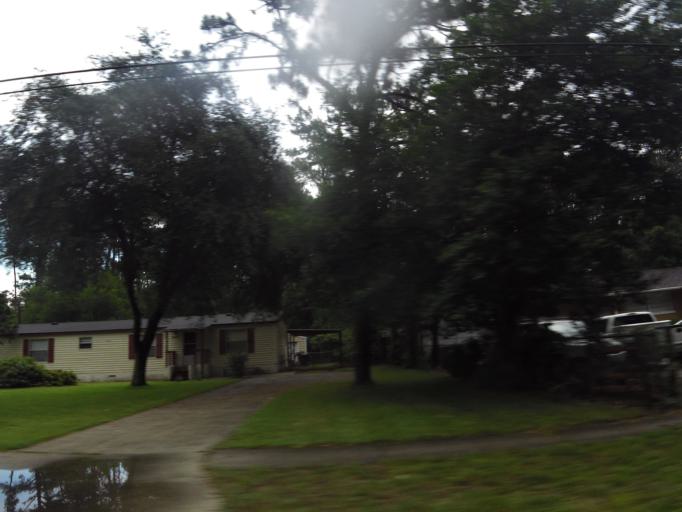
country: US
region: Florida
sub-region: Duval County
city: Jacksonville
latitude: 30.3112
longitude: -81.5419
